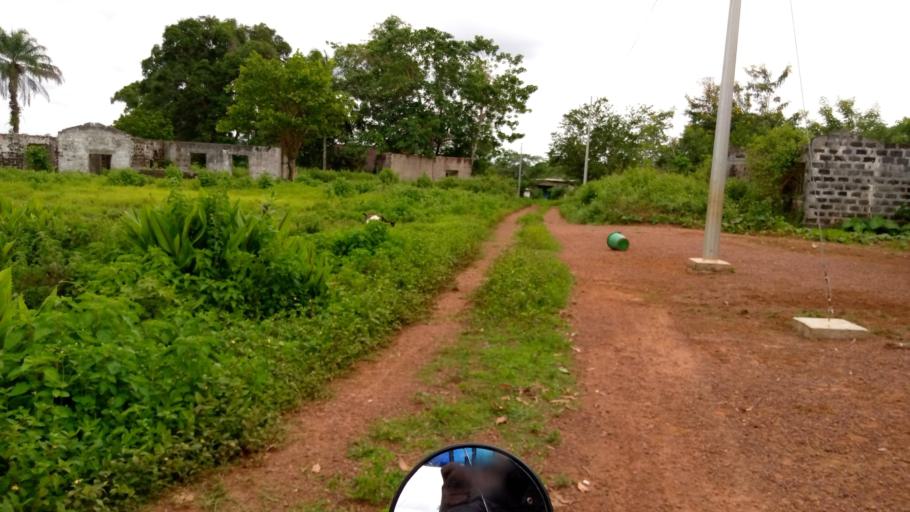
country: SL
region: Southern Province
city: Rotifunk
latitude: 8.1922
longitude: -12.5656
